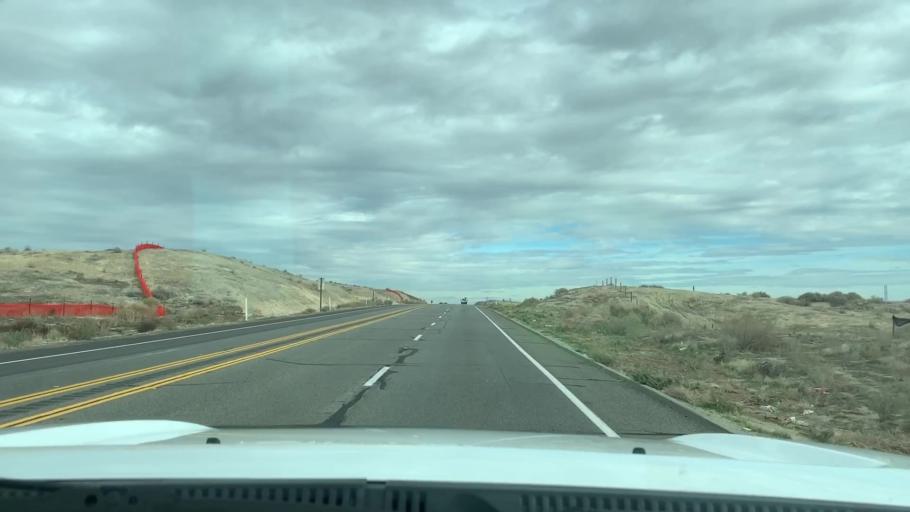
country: US
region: California
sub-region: Kern County
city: Ford City
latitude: 35.2540
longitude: -119.3330
